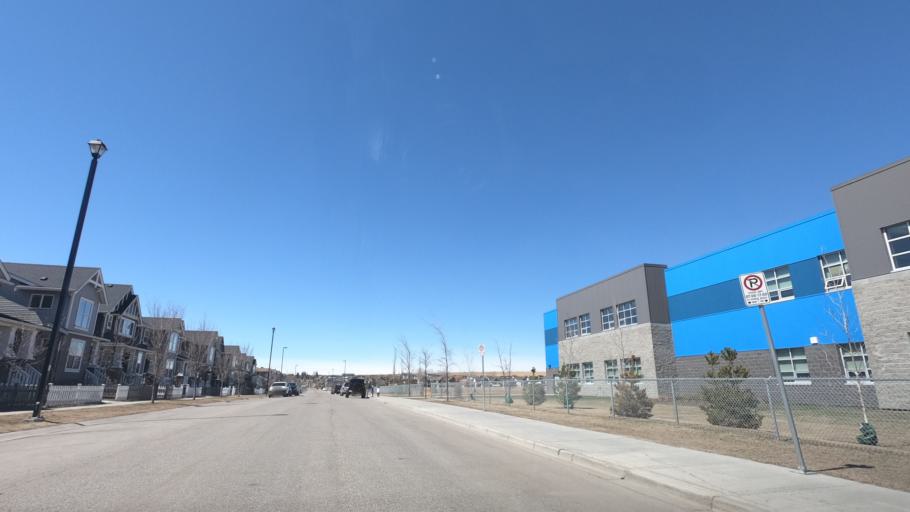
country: CA
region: Alberta
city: Airdrie
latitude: 51.3030
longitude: -114.0354
